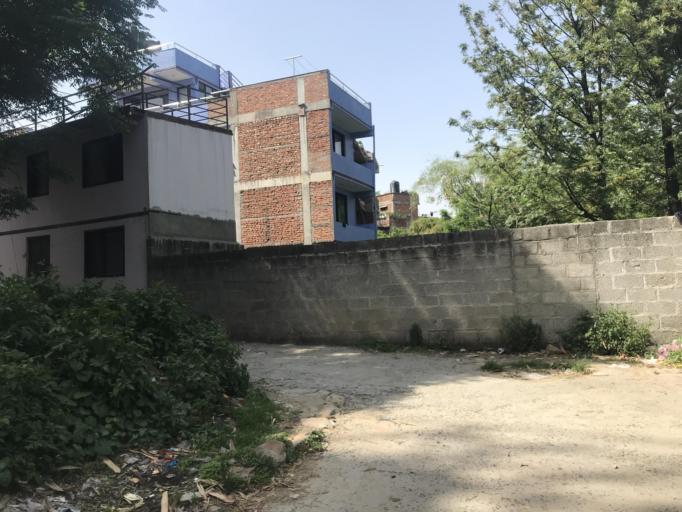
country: NP
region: Central Region
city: Kirtipur
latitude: 27.6762
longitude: 85.2796
